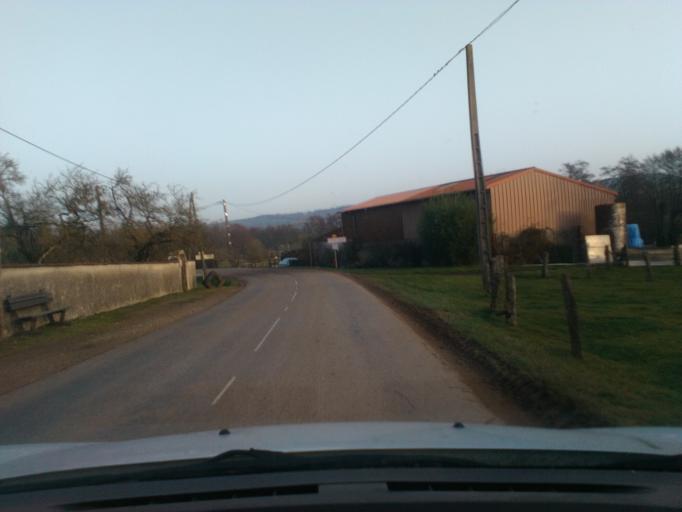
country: FR
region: Lorraine
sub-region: Departement des Vosges
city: Mirecourt
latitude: 48.2776
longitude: 6.0344
